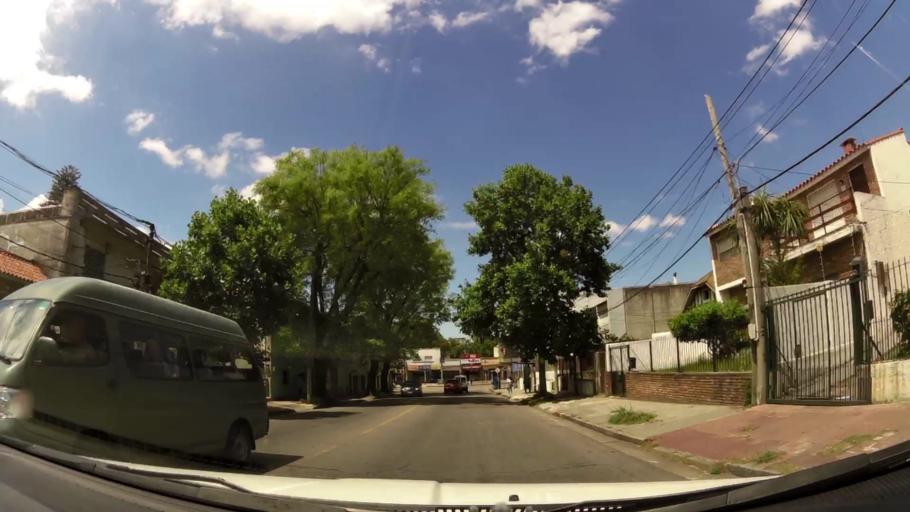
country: UY
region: Montevideo
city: Montevideo
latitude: -34.8498
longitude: -56.1991
